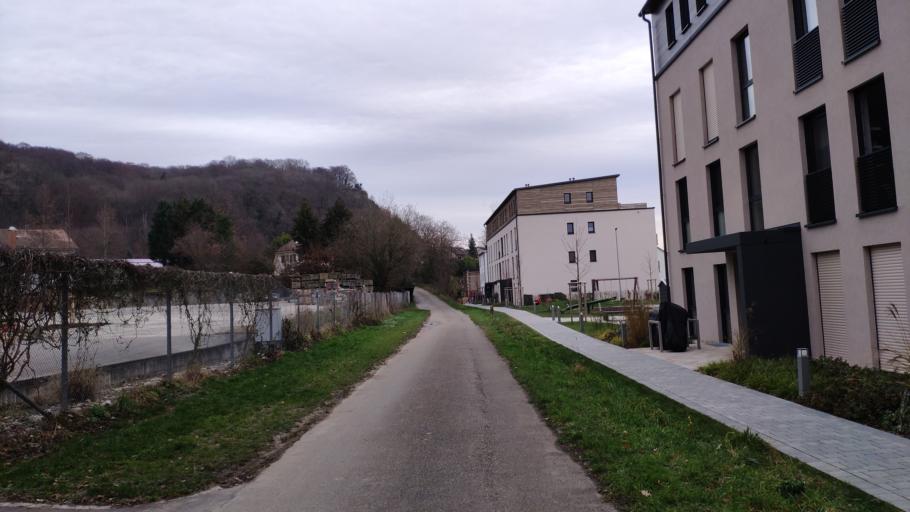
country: CH
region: Basel-City
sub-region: Basel-Stadt
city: Riehen
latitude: 47.5623
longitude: 7.6397
